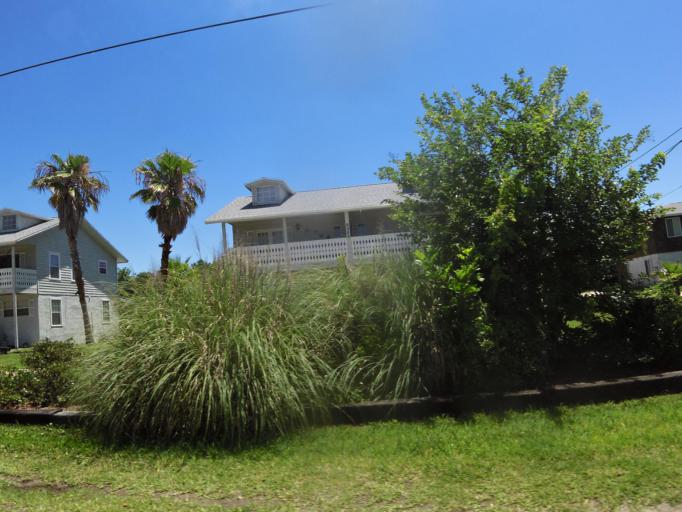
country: US
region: Florida
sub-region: Saint Johns County
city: Butler Beach
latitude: 29.7667
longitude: -81.2541
